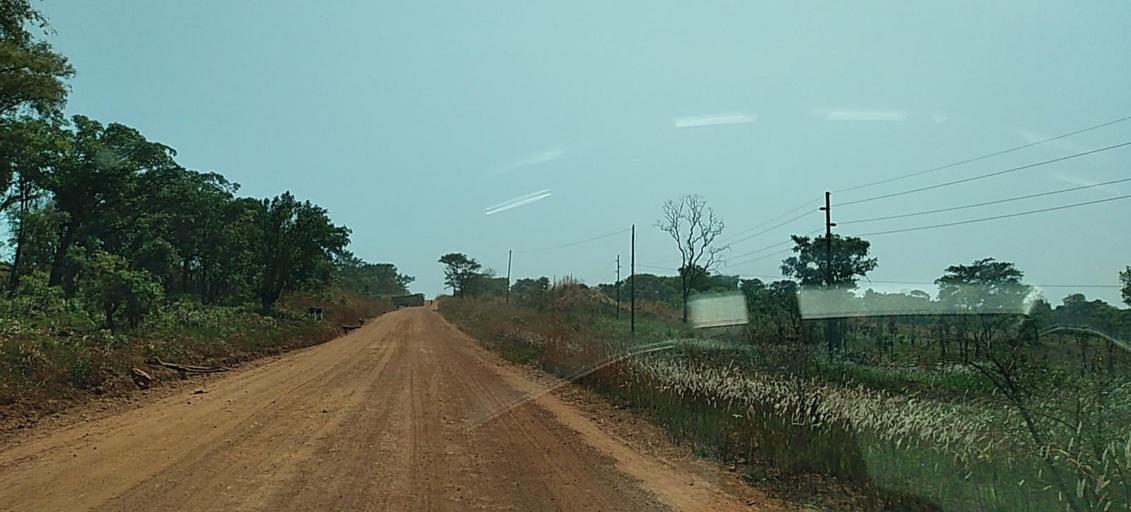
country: ZM
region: North-Western
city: Kansanshi
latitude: -12.0071
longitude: 26.5789
